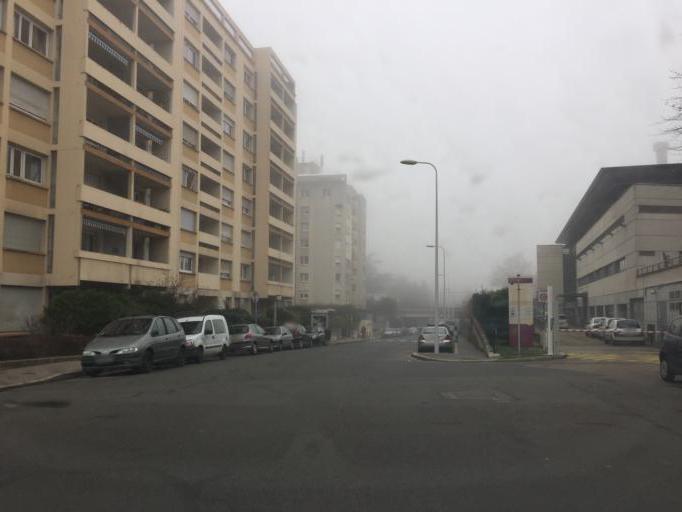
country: FR
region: Rhone-Alpes
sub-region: Departement du Rhone
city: Caluire-et-Cuire
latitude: 45.7811
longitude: 4.8292
